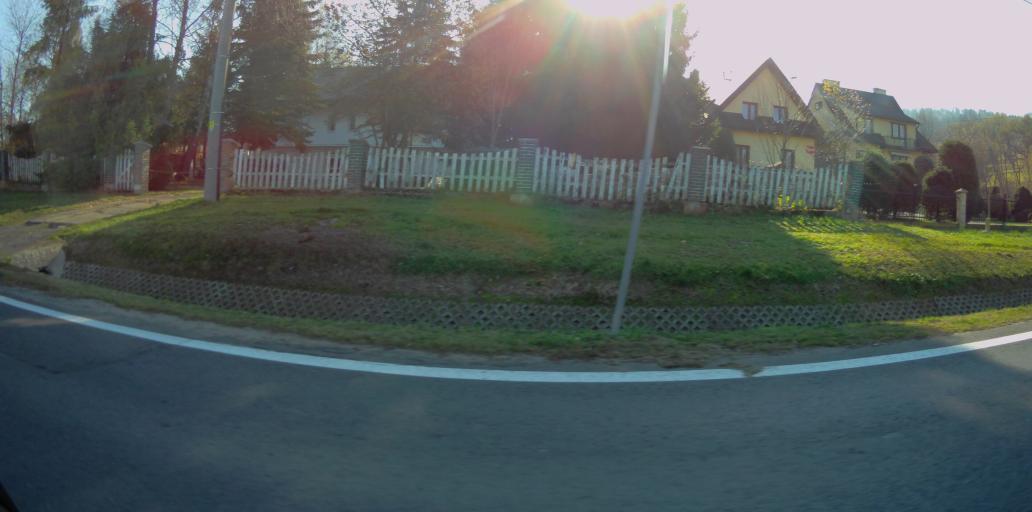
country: PL
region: Subcarpathian Voivodeship
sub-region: Powiat bieszczadzki
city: Ustrzyki Dolne
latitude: 49.4421
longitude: 22.6144
